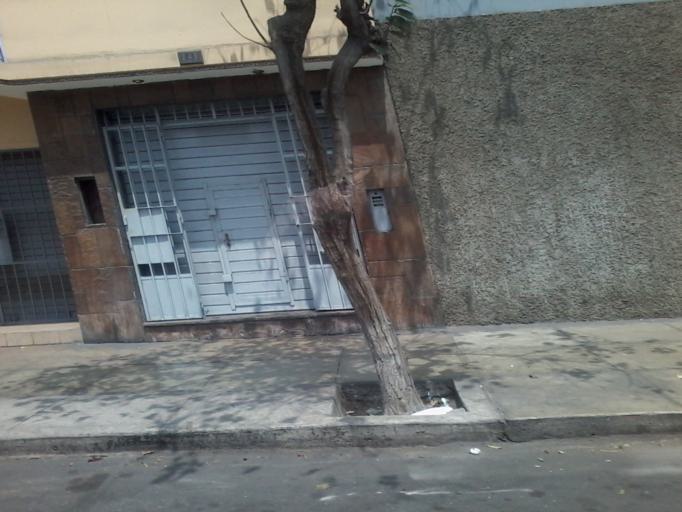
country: PE
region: Lima
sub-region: Lima
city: San Isidro
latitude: -12.0850
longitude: -77.0368
